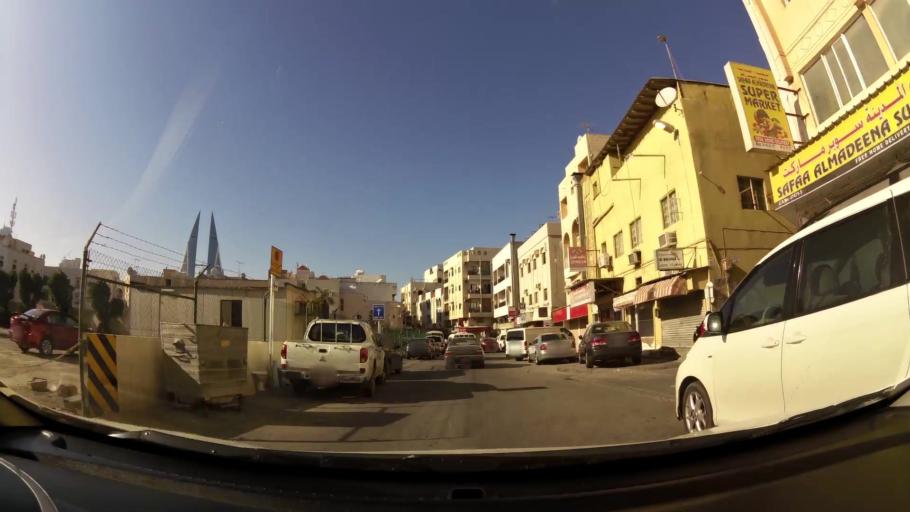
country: BH
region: Manama
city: Manama
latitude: 26.2332
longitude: 50.5873
